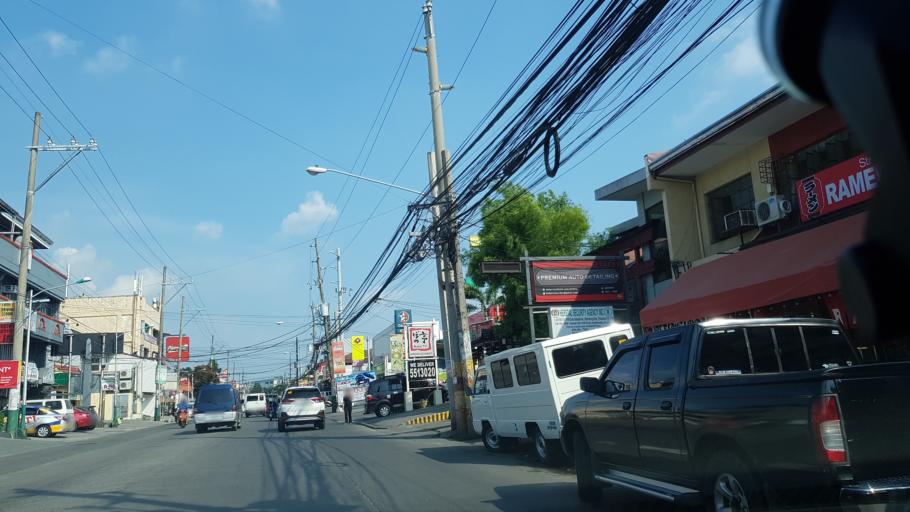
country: PH
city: Sambayanihan People's Village
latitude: 14.4840
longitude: 121.0326
